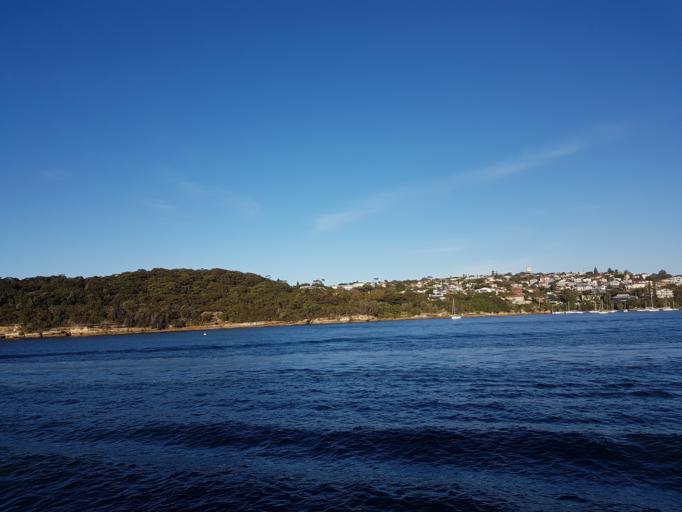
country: AU
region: New South Wales
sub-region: Woollahra
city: Point Piper
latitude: -33.8538
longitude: 151.2614
